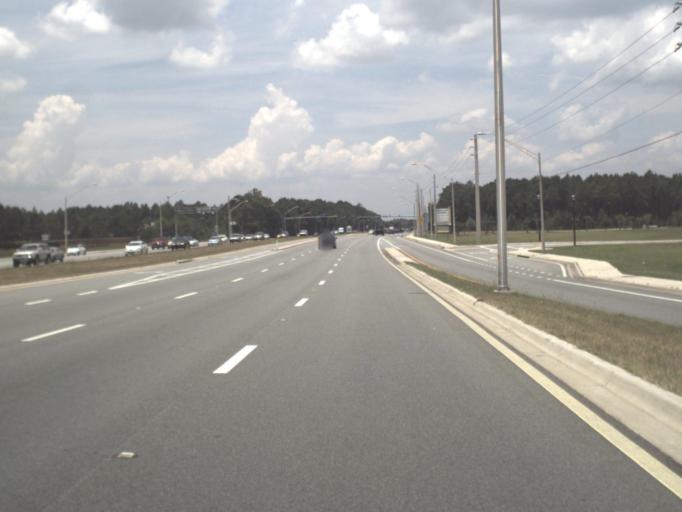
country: US
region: Florida
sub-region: Duval County
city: Atlantic Beach
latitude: 30.3206
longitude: -81.4933
